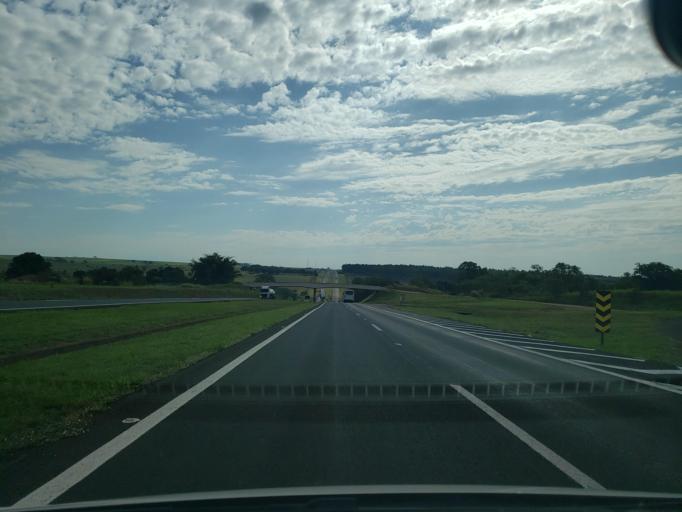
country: BR
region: Sao Paulo
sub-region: Promissao
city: Promissao
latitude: -21.6136
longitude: -49.8652
